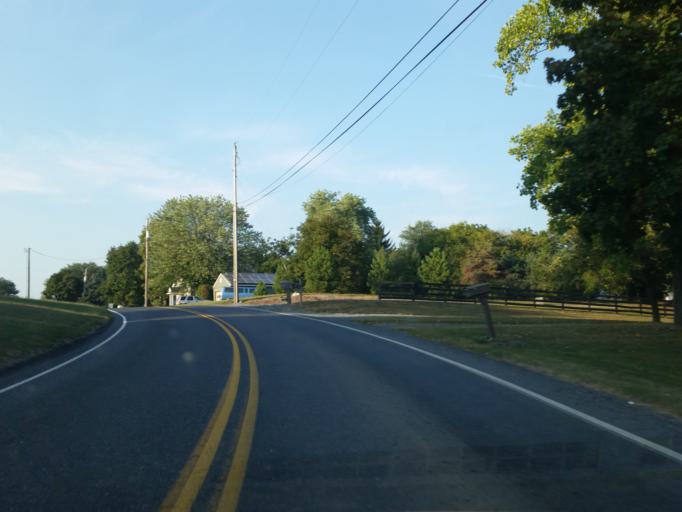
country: US
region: Pennsylvania
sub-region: Lebanon County
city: Annville
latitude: 40.3359
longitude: -76.5403
